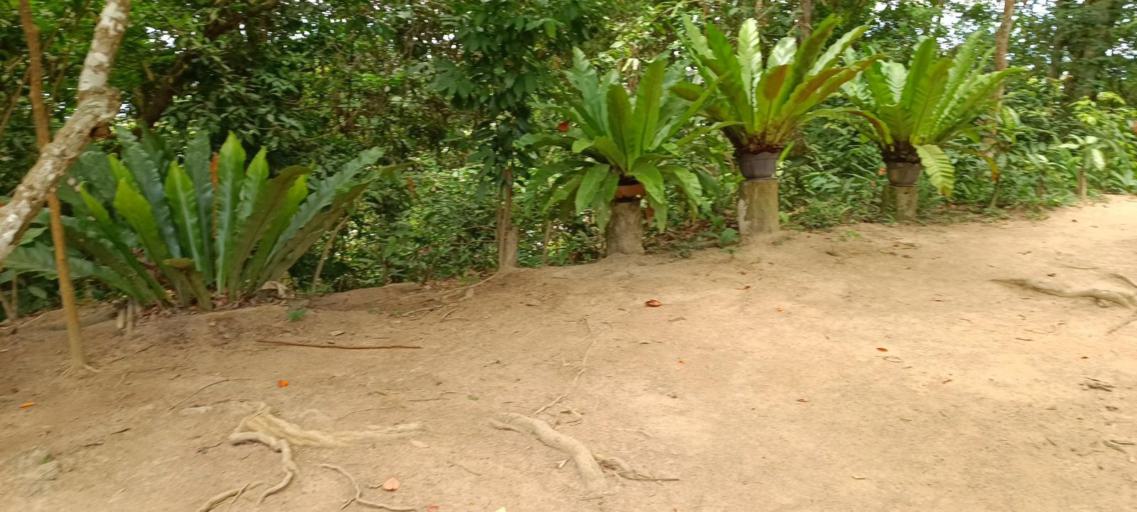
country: MY
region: Penang
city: Kampung Sungai Ara
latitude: 5.3538
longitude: 100.2819
